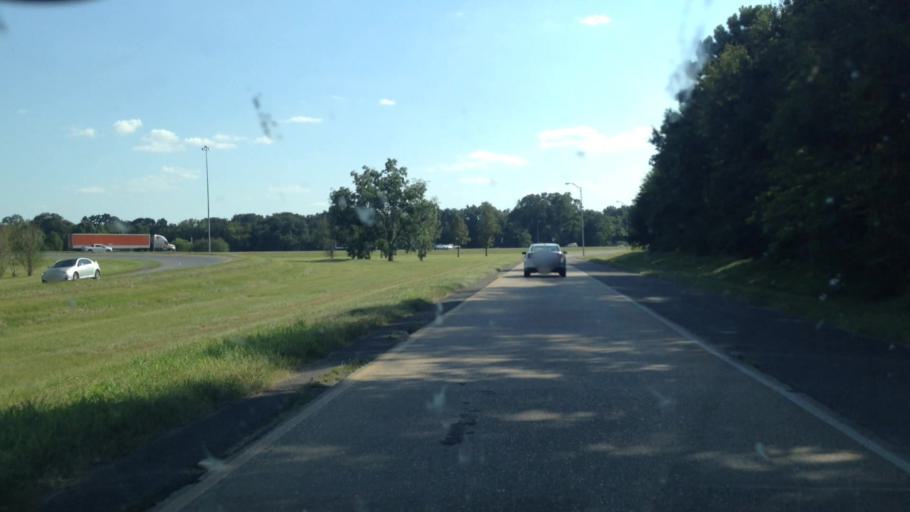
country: US
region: Louisiana
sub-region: Lafayette Parish
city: Lafayette
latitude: 30.2608
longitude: -92.0178
